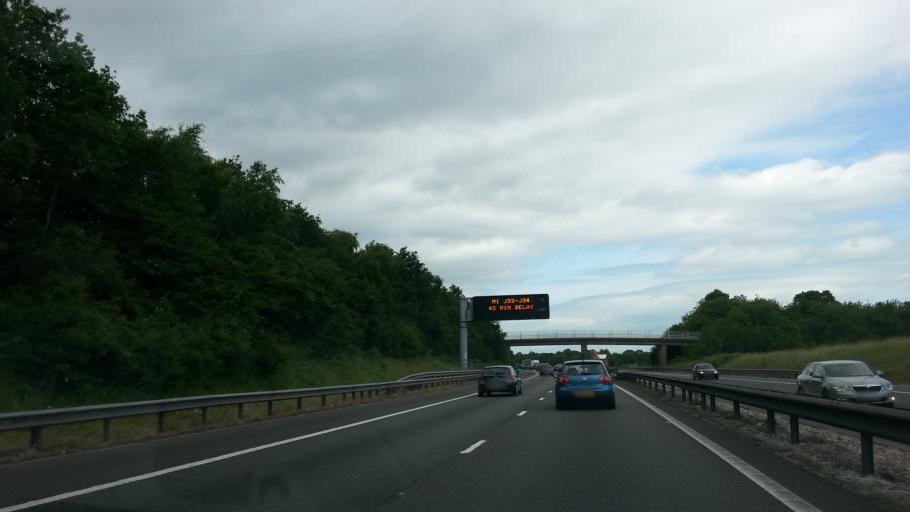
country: GB
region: England
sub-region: Warwickshire
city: Kingsbury
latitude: 52.5834
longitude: -1.6653
